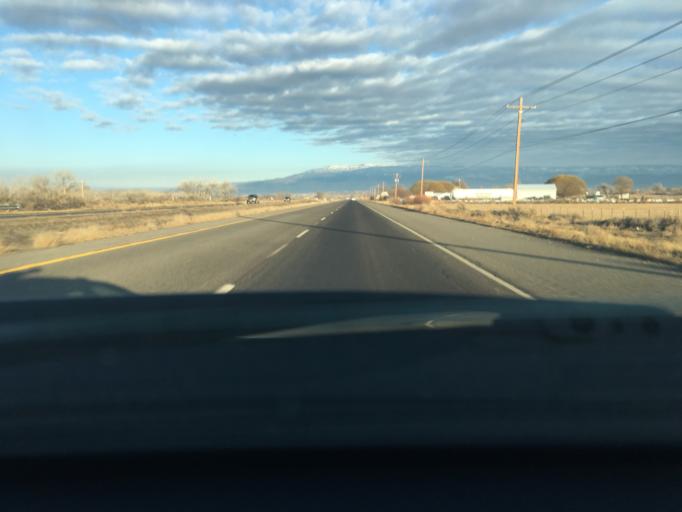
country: US
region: Colorado
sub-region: Montrose County
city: Olathe
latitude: 38.6699
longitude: -107.9999
